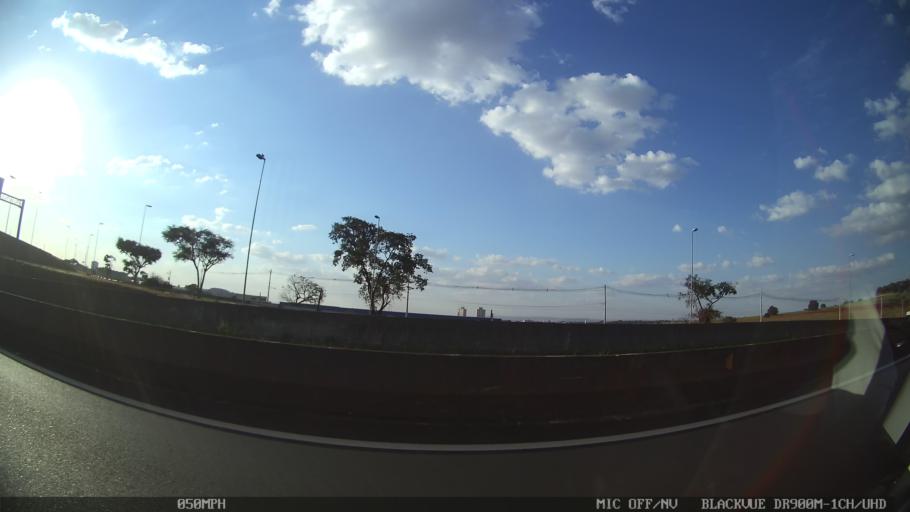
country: BR
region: Sao Paulo
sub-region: Ribeirao Preto
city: Ribeirao Preto
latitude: -21.2061
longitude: -47.7555
